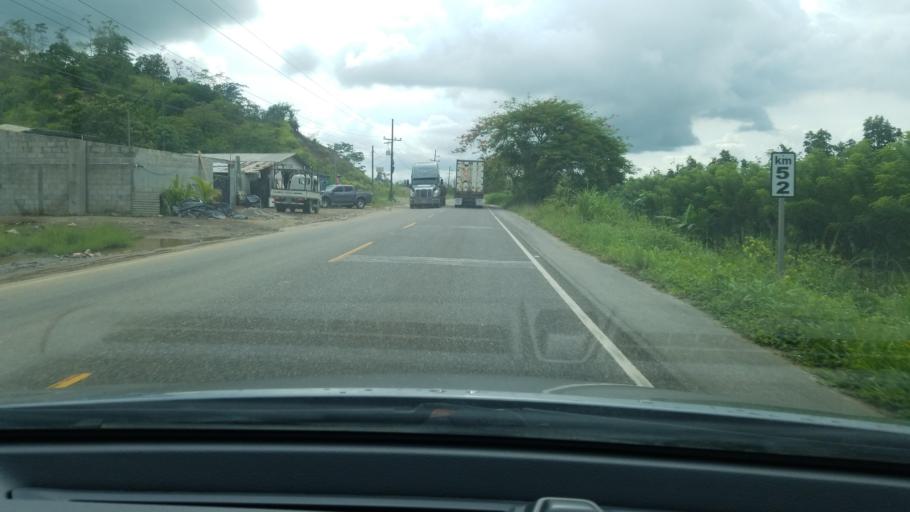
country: HN
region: Cortes
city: Potrerillos
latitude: 15.5948
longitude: -88.3134
